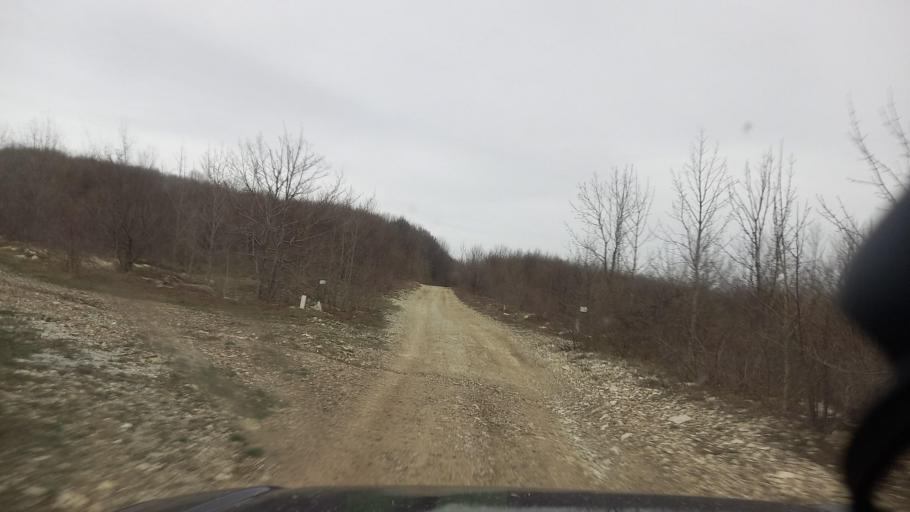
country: RU
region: Krasnodarskiy
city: Pshada
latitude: 44.5977
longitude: 38.2877
